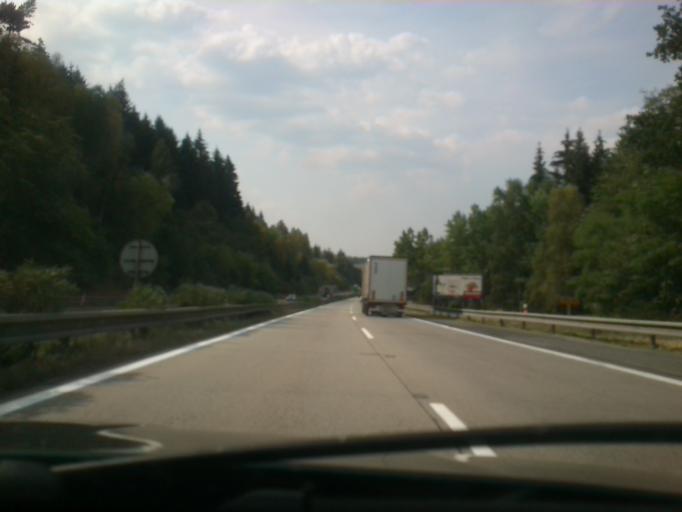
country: CZ
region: Central Bohemia
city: Divisov
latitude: 49.8128
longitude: 14.8817
